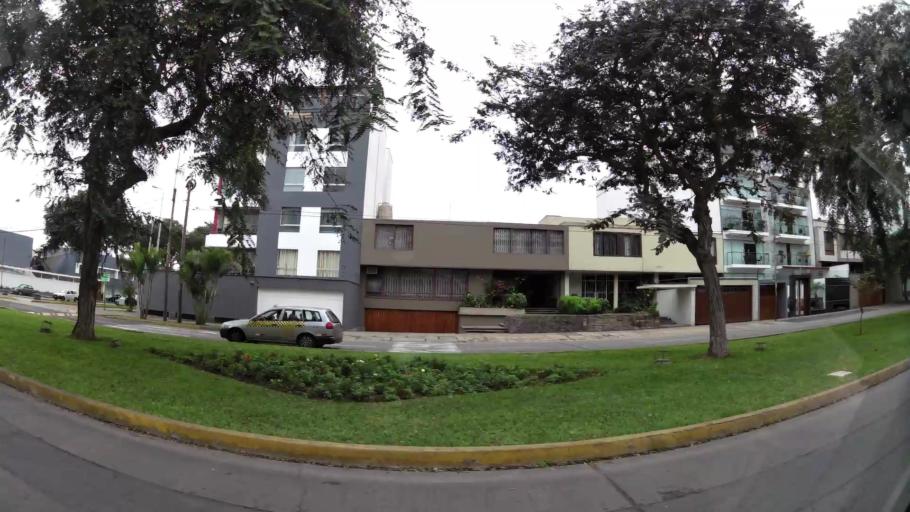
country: PE
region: Lima
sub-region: Lima
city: Surco
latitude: -12.1228
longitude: -77.0129
